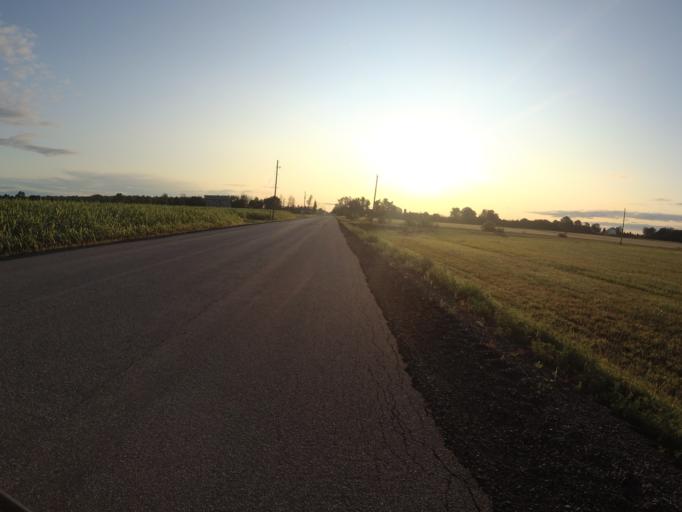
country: CA
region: Ontario
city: Ottawa
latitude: 45.1362
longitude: -75.4671
